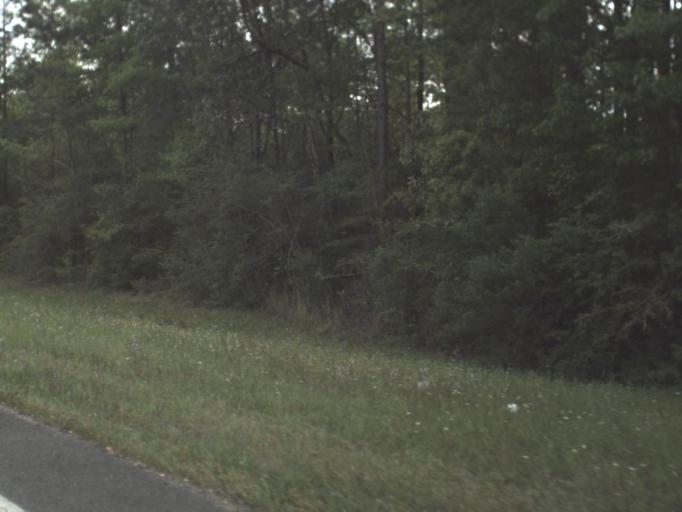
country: US
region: Florida
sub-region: Escambia County
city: Molino
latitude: 30.6897
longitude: -87.3510
